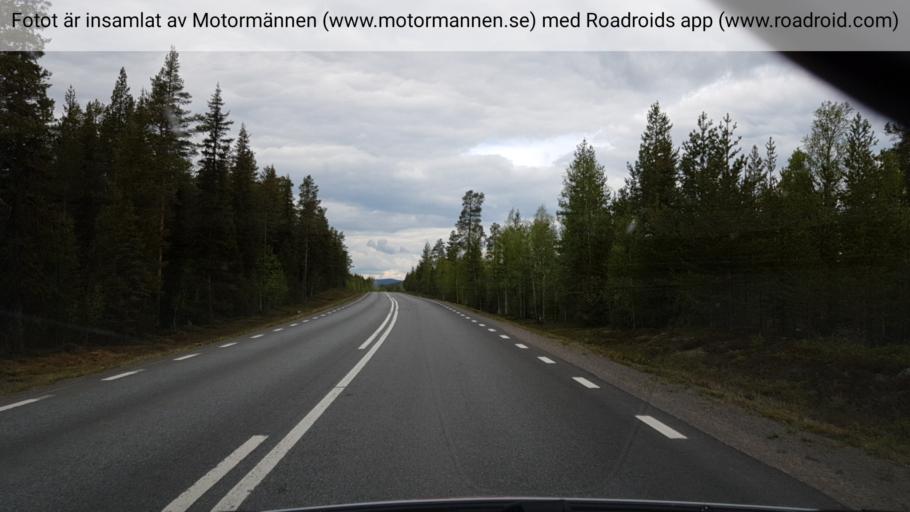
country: SE
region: Norrbotten
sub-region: Arvidsjaurs Kommun
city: Arvidsjaur
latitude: 65.5137
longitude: 19.2778
